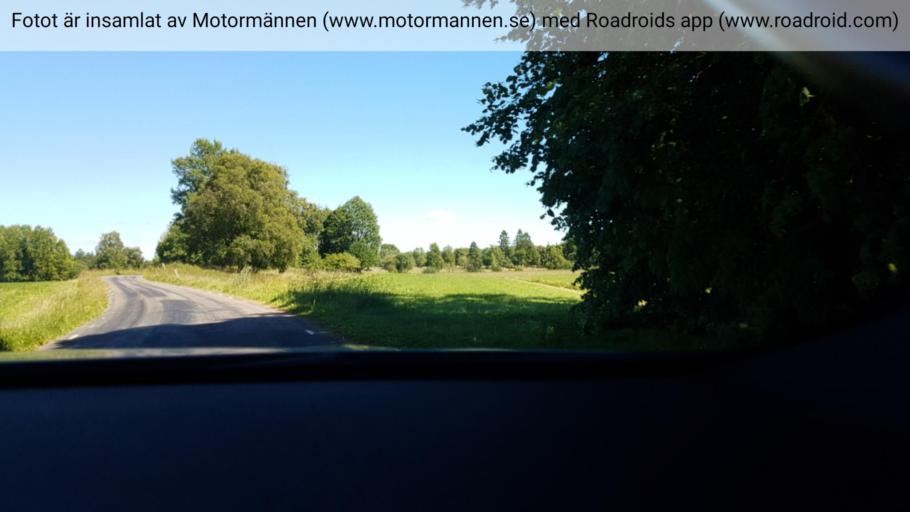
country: SE
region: Vaestra Goetaland
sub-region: Falkopings Kommun
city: Falkoeping
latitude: 58.0693
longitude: 13.5338
